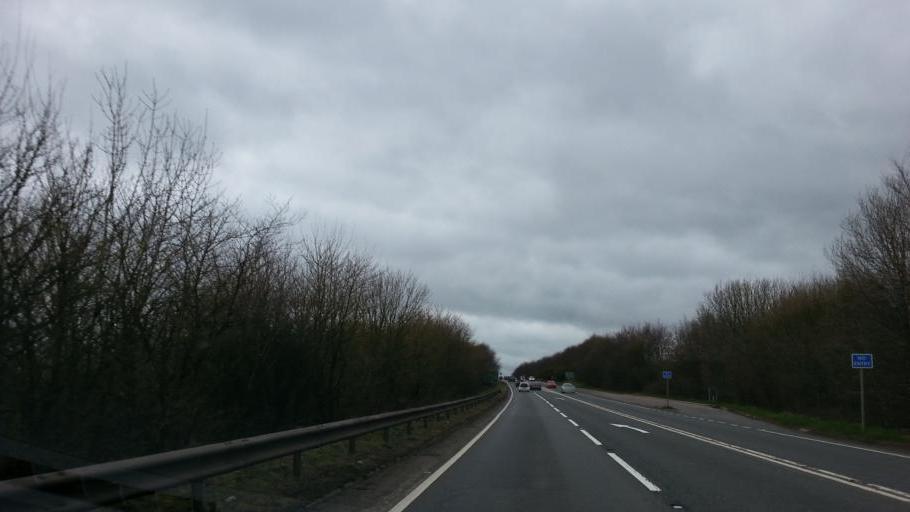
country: GB
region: England
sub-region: Devon
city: Tiverton
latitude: 50.9396
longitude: -3.5598
